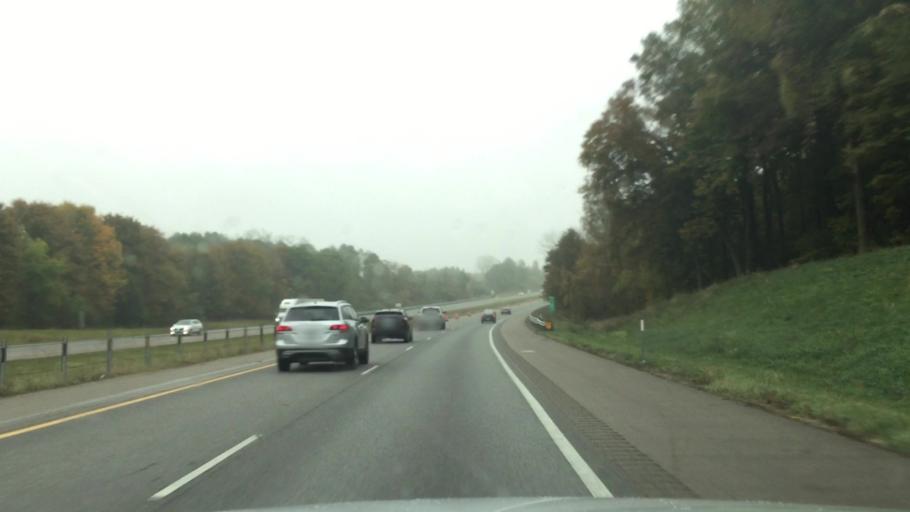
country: US
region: Michigan
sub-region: Van Buren County
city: Hartford
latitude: 42.1971
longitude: -86.1014
